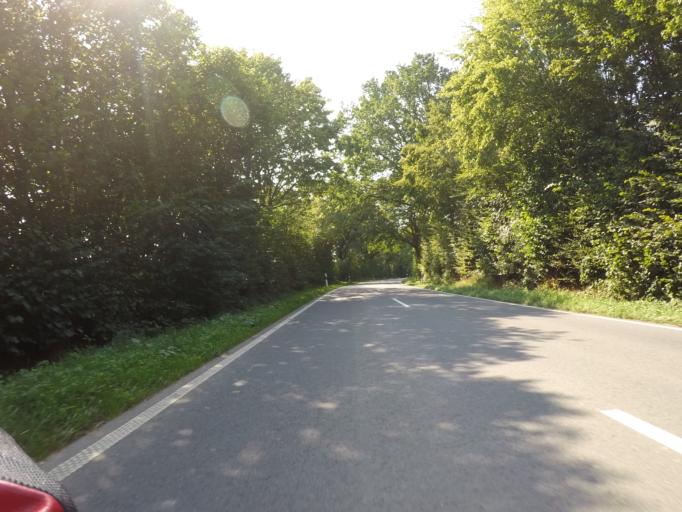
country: DE
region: Schleswig-Holstein
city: Huttblek
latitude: 53.8435
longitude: 10.0674
